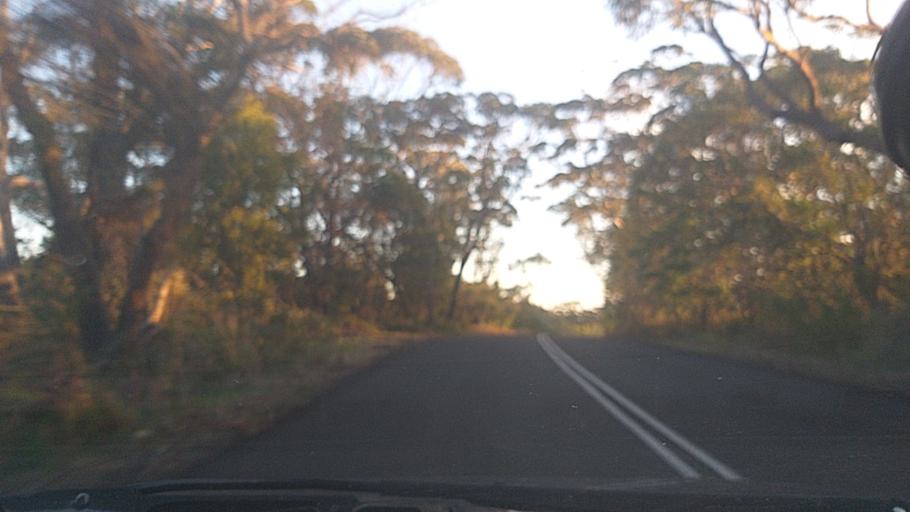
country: AU
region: New South Wales
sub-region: Wollongong
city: Mount Keira
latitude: -34.3898
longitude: 150.8412
